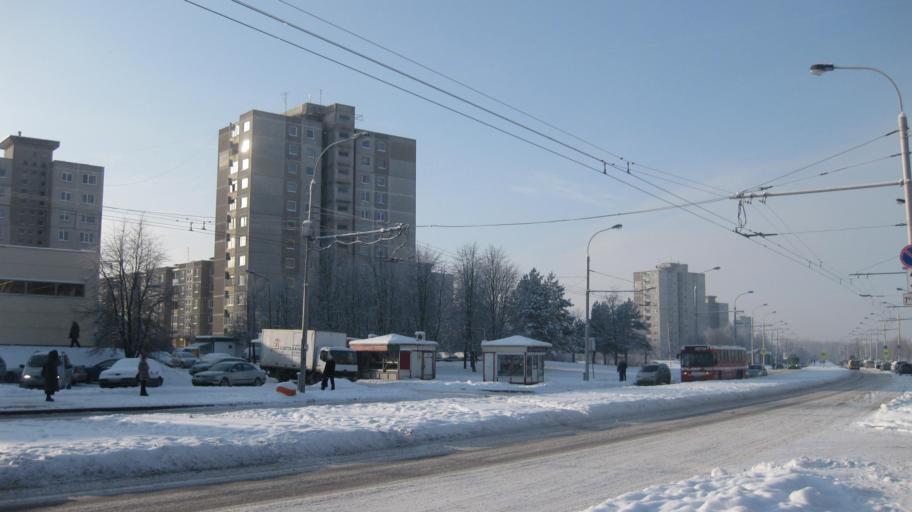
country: LT
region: Kauno apskritis
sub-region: Kaunas
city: Eiguliai
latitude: 54.9314
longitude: 23.9363
